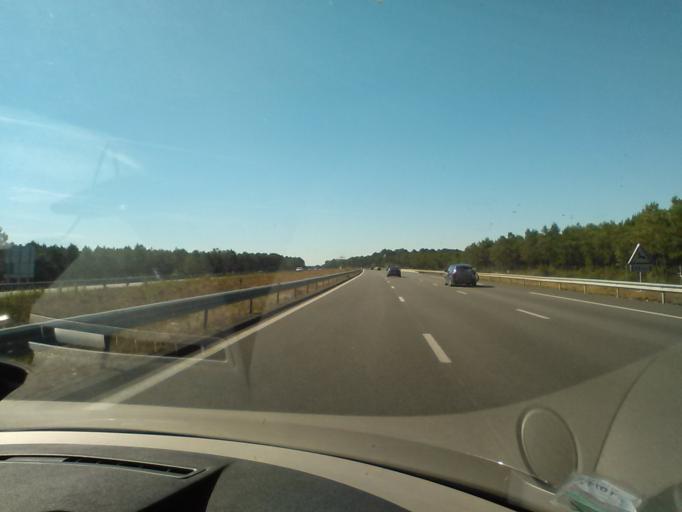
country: FR
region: Aquitaine
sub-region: Departement de la Gironde
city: Belin-Beliet
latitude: 44.4959
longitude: -0.8398
